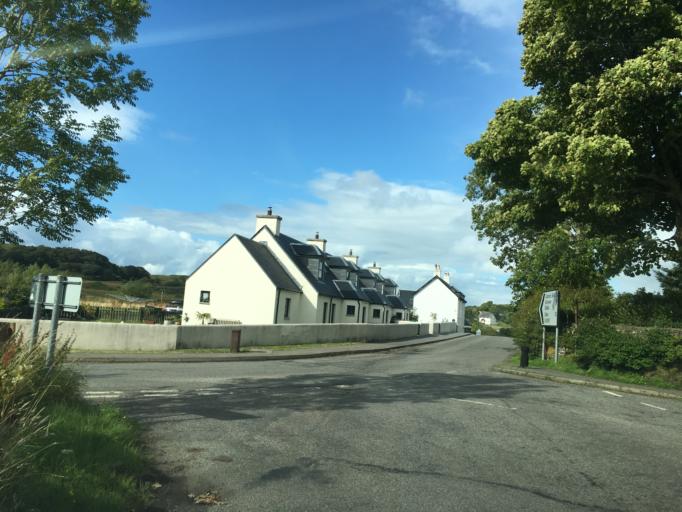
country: GB
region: Scotland
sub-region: Argyll and Bute
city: Oban
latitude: 56.2909
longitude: -5.6156
